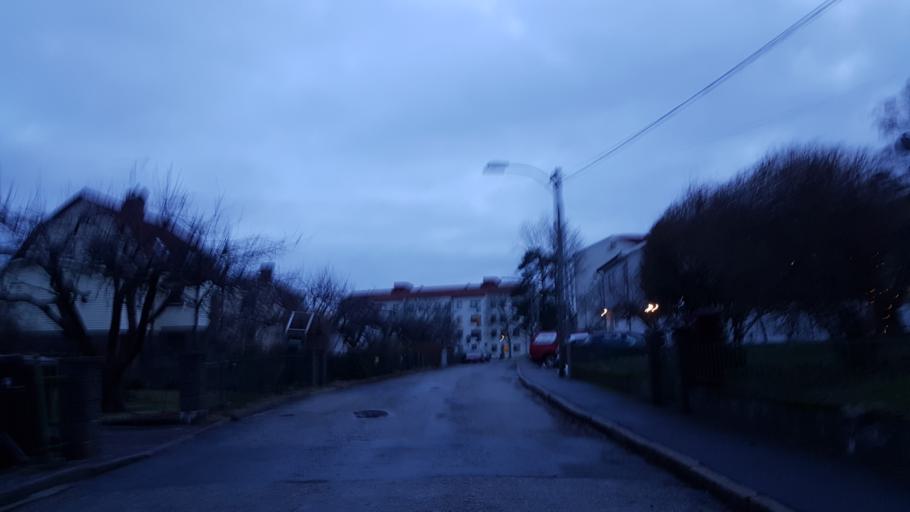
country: SE
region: Stockholm
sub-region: Stockholms Kommun
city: Arsta
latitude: 59.2759
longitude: 18.0519
